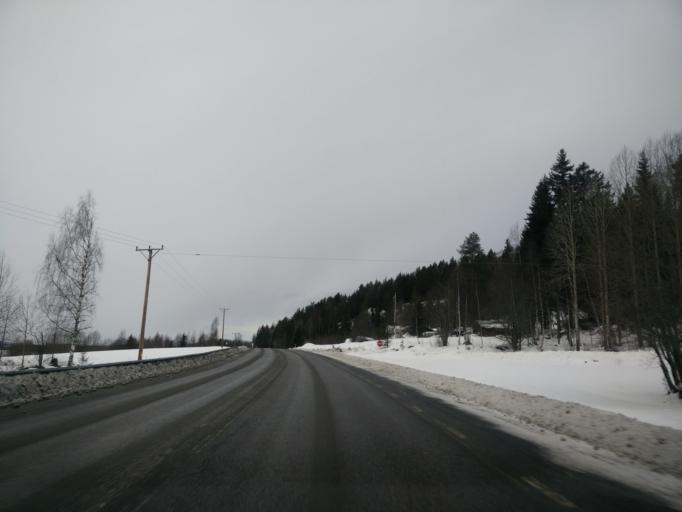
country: SE
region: Vaesternorrland
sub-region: Sundsvalls Kommun
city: Matfors
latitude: 62.4164
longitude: 16.6344
